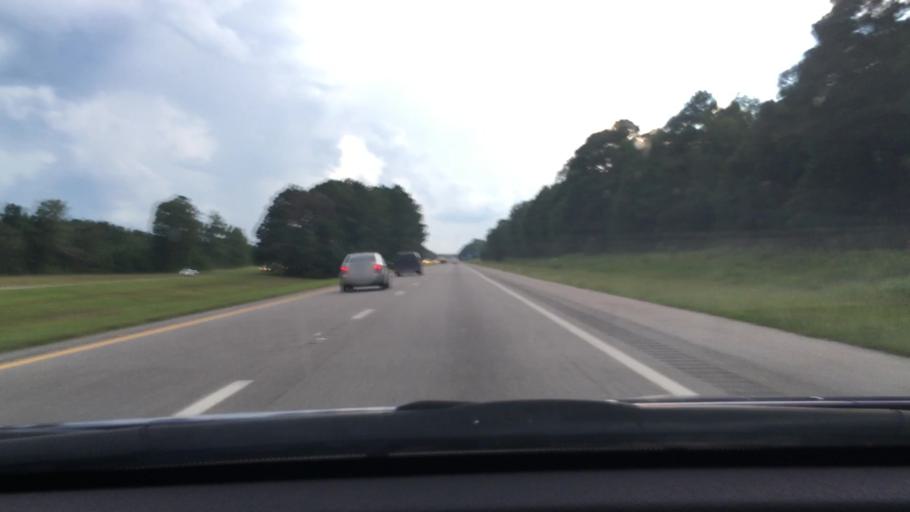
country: US
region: South Carolina
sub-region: Kershaw County
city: Camden
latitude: 34.2138
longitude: -80.5627
